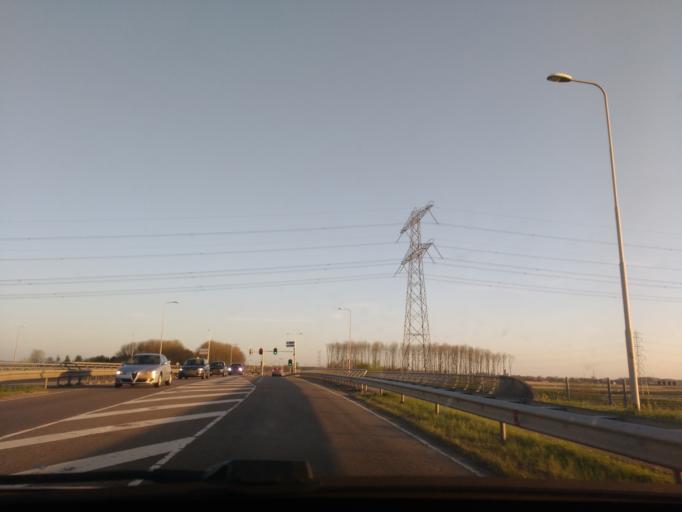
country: NL
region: Gelderland
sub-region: Gemeente Overbetuwe
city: Oosterhout
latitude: 51.8964
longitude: 5.8365
